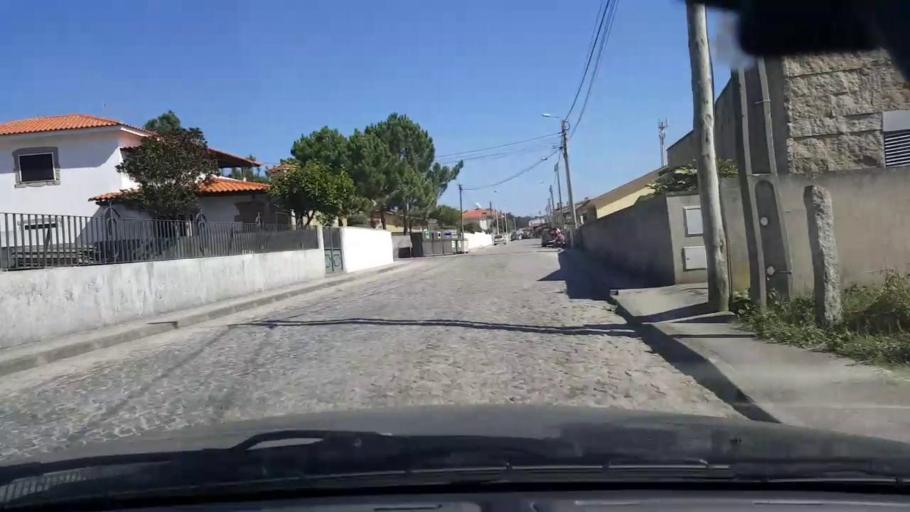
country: PT
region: Porto
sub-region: Matosinhos
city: Lavra
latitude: 41.2980
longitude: -8.7285
